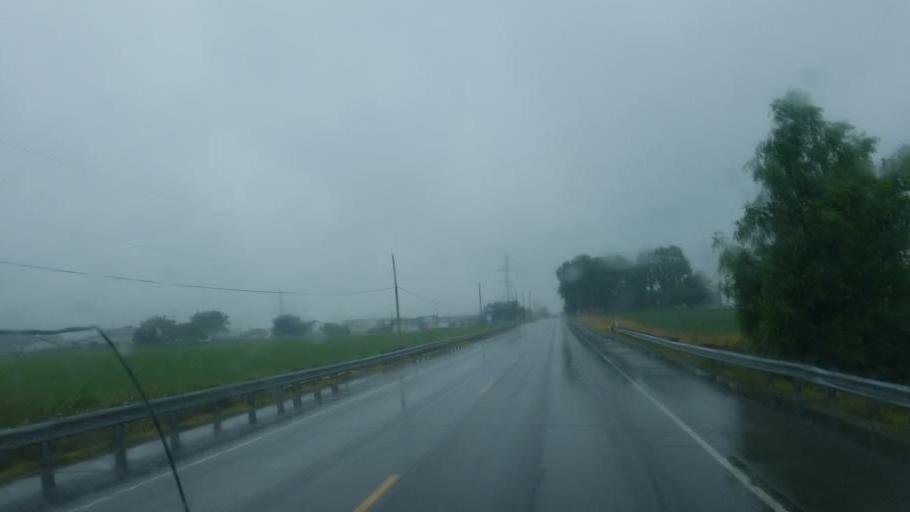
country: US
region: Indiana
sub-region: Allen County
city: Grabill
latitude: 41.1531
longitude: -84.9824
